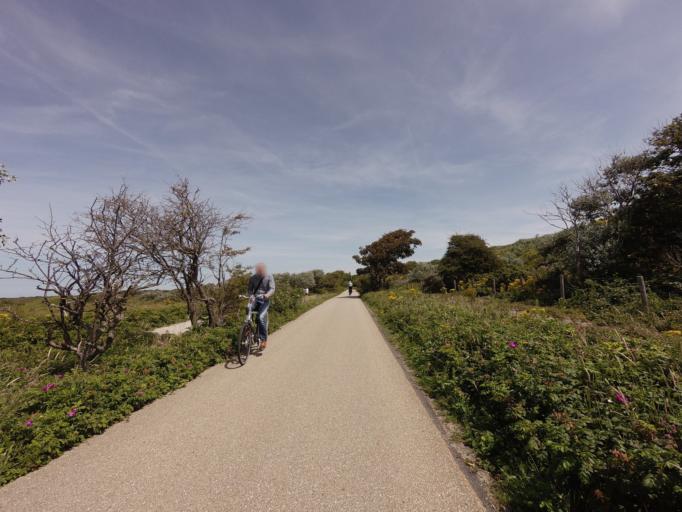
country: NL
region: South Holland
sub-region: Gemeente Den Haag
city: Scheveningen
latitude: 52.0847
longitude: 4.2458
